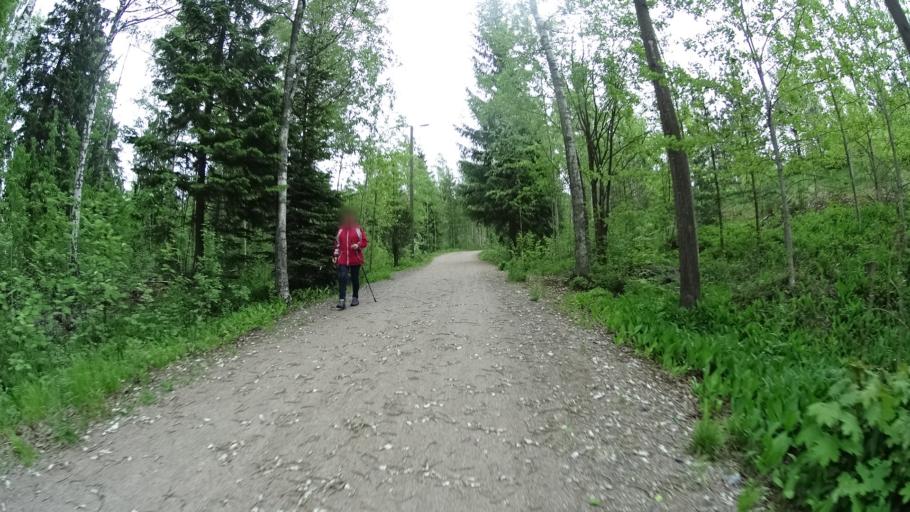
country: FI
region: Uusimaa
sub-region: Helsinki
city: Vantaa
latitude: 60.2517
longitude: 25.0711
